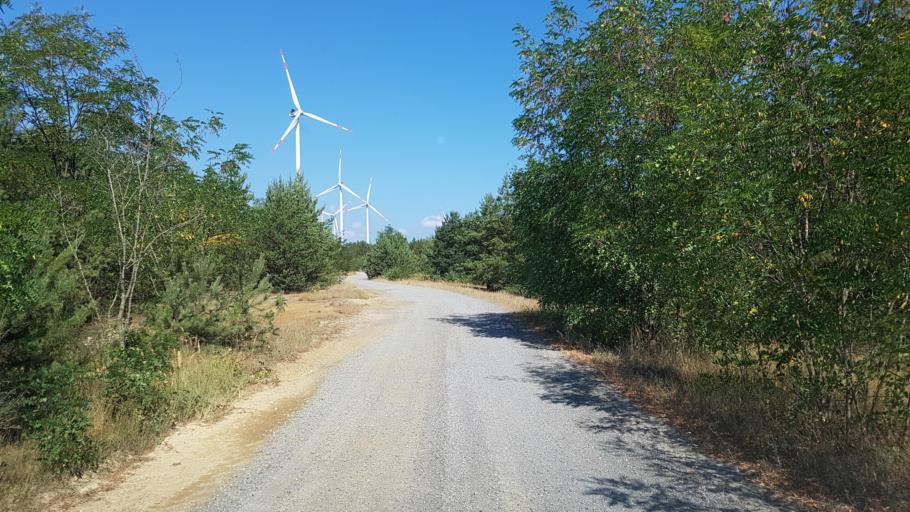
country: DE
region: Brandenburg
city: Schipkau
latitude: 51.5403
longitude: 13.8631
